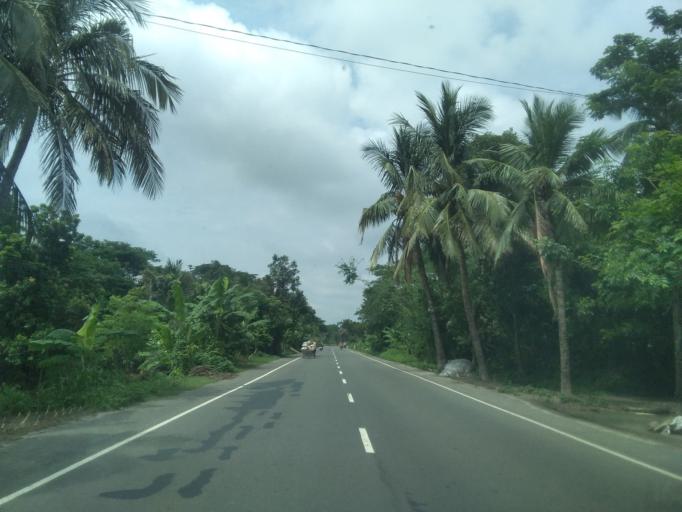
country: BD
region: Khulna
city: Kesabpur
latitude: 22.8187
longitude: 89.2611
